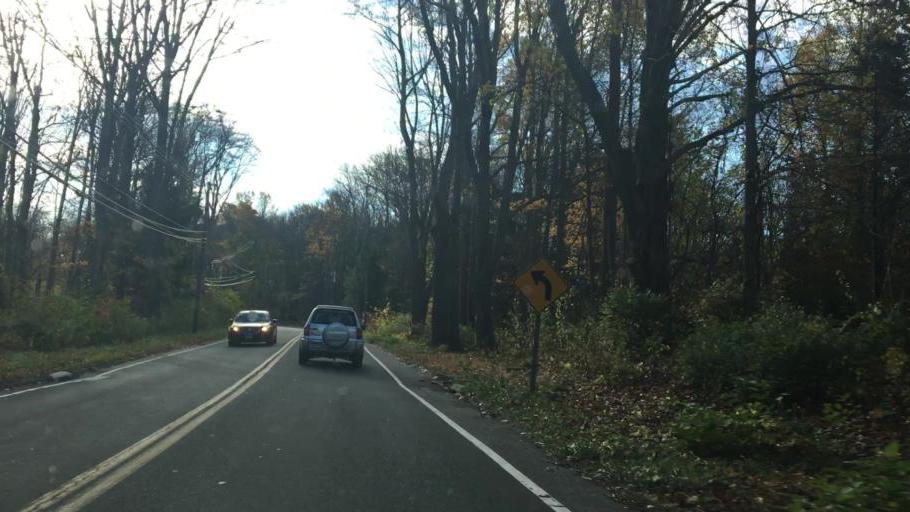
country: US
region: Connecticut
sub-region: New Haven County
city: Ansonia
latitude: 41.3742
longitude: -73.1246
